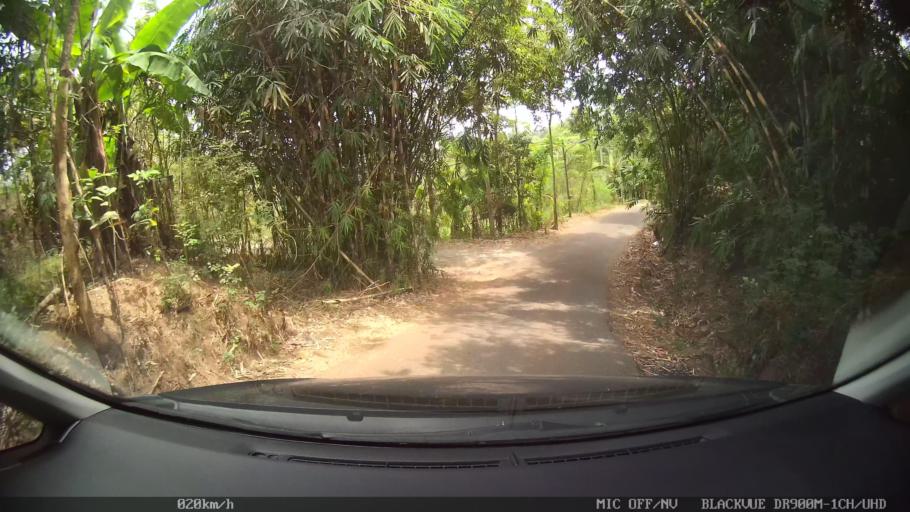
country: ID
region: Central Java
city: Candi Prambanan
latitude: -7.7945
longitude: 110.5192
